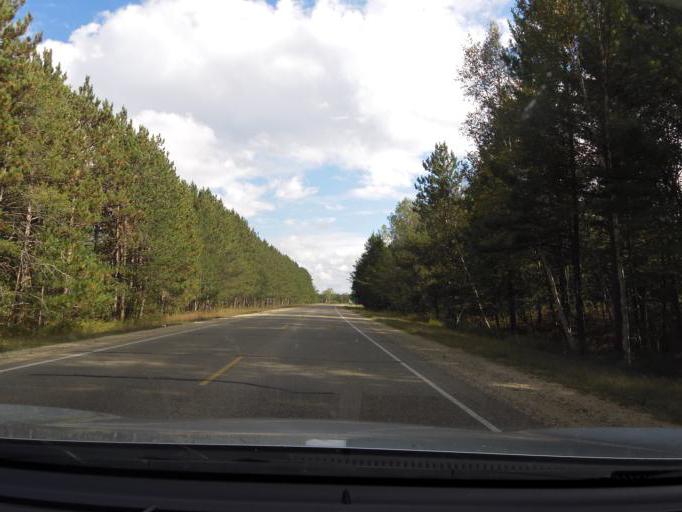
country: US
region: Michigan
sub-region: Roscommon County
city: Saint Helen
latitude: 44.4082
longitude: -84.4537
